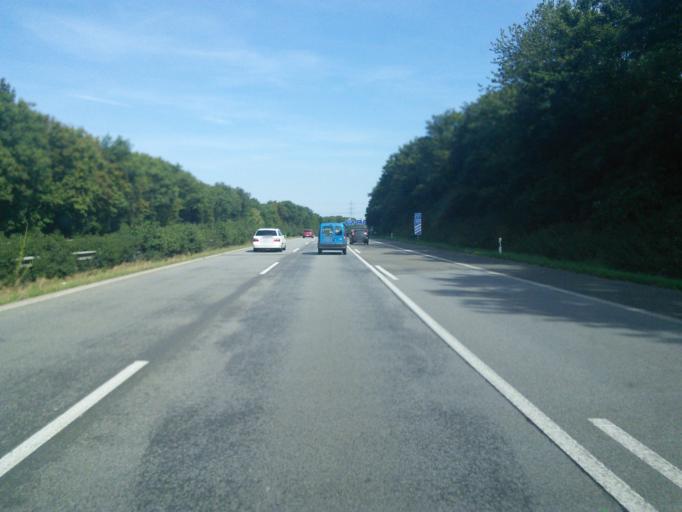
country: DE
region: North Rhine-Westphalia
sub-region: Regierungsbezirk Dusseldorf
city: Kaarst
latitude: 51.2372
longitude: 6.6198
